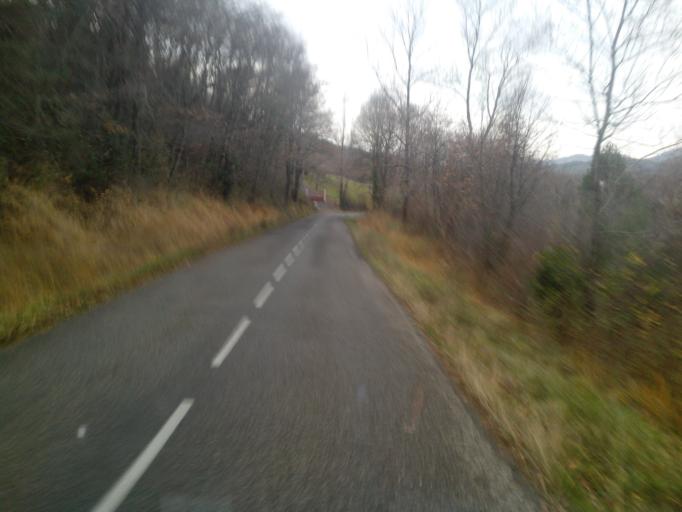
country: FR
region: Midi-Pyrenees
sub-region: Departement de l'Ariege
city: Varilhes
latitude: 43.0336
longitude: 1.5396
